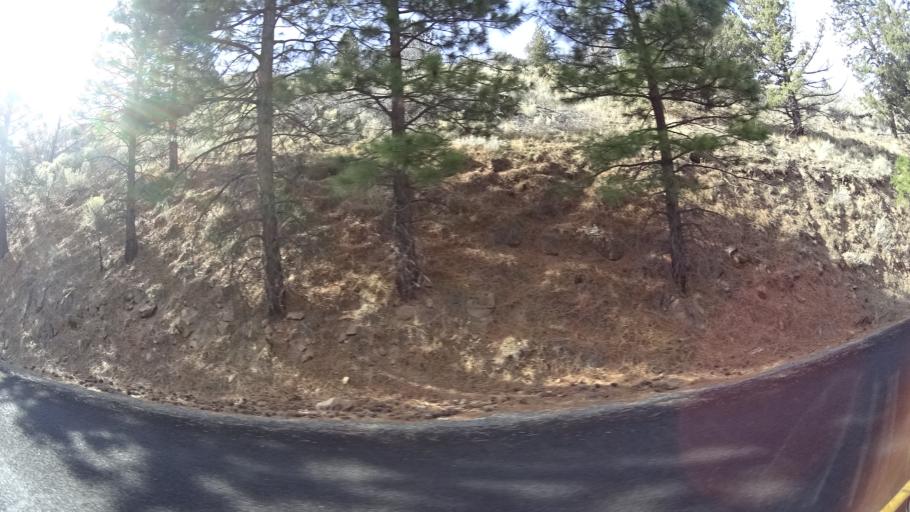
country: US
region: California
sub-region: Siskiyou County
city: Weed
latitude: 41.5026
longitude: -122.3904
